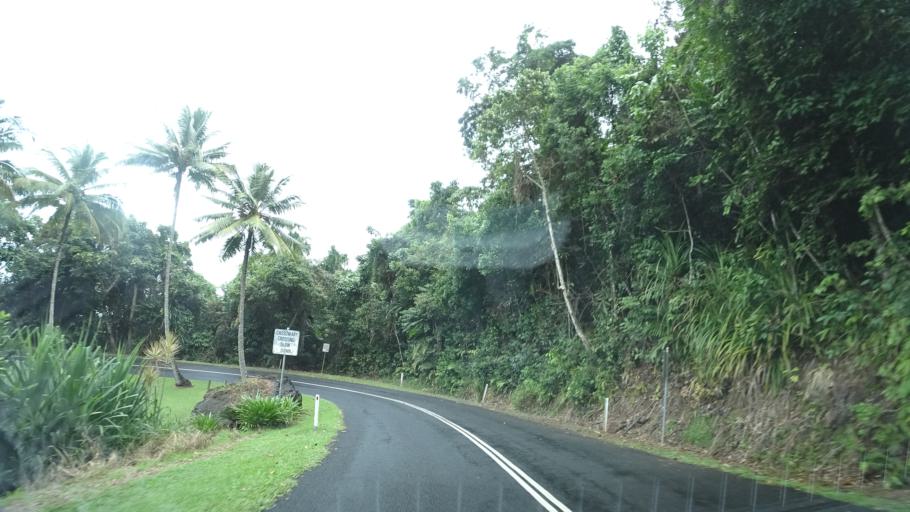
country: AU
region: Queensland
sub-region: Cassowary Coast
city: Innisfail
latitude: -17.5602
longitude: 146.0896
